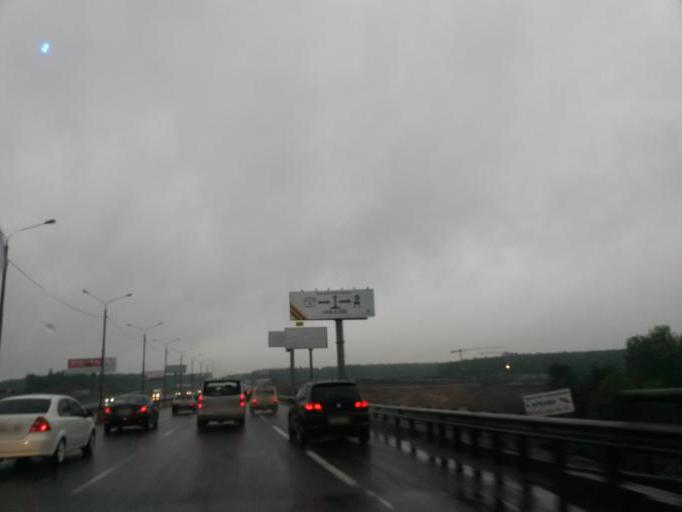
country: RU
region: Moscow
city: Annino
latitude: 55.5280
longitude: 37.6103
